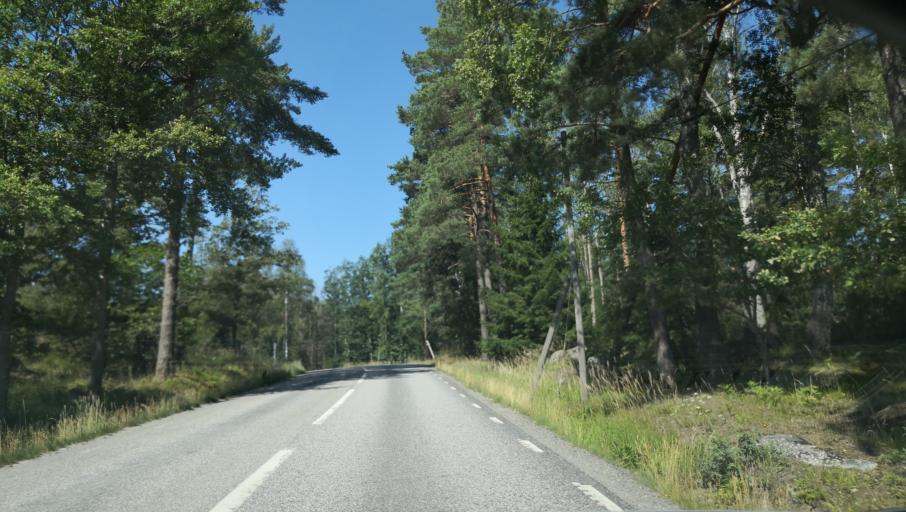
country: SE
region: Stockholm
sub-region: Varmdo Kommun
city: Hemmesta
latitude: 59.3905
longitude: 18.5050
